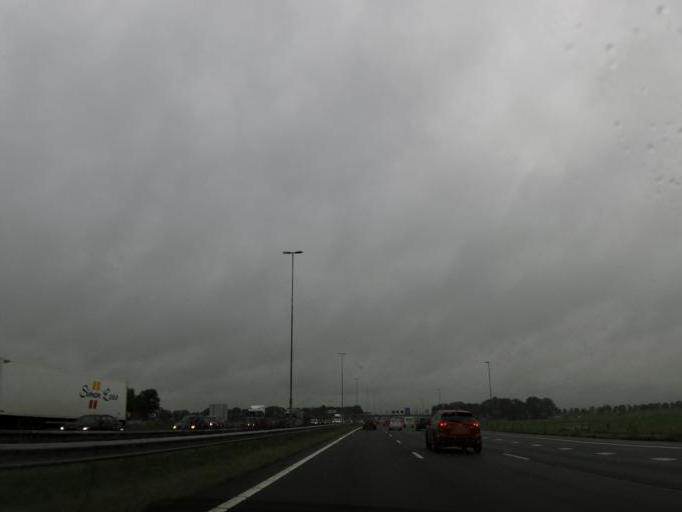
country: NL
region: Gelderland
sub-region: Gemeente Zaltbommel
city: Zaltbommel
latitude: 51.7843
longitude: 5.2583
